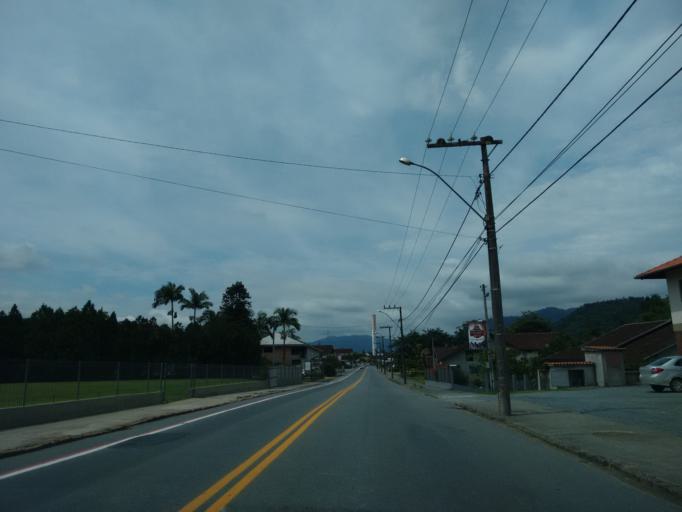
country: BR
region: Santa Catarina
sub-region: Pomerode
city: Pomerode
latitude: -26.7004
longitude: -49.1608
